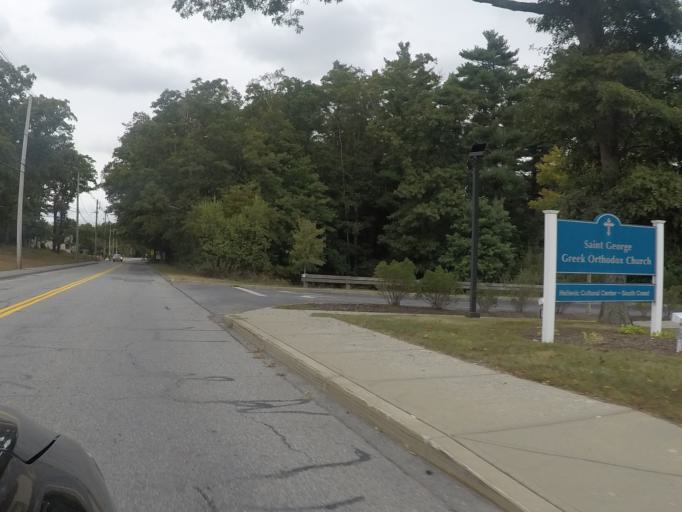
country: US
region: Massachusetts
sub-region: Bristol County
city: Smith Mills
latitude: 41.6453
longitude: -71.0072
